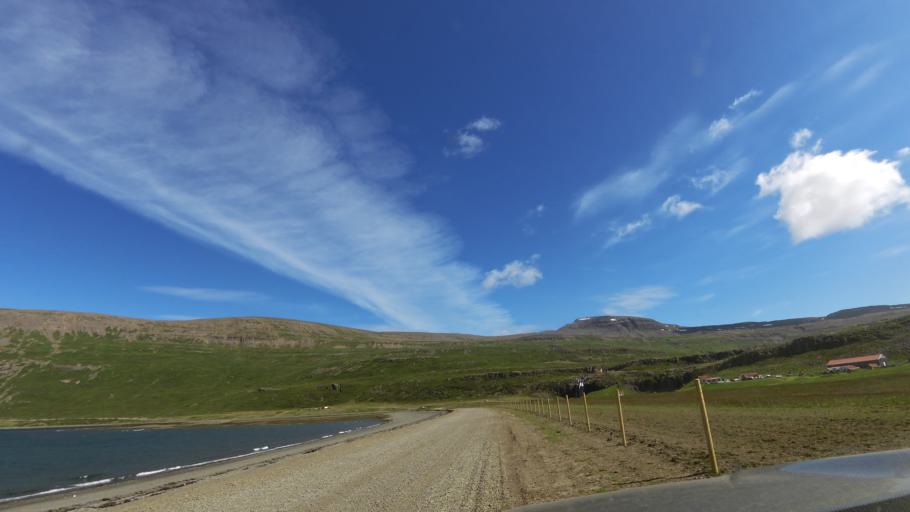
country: IS
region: Westfjords
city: Isafjoerdur
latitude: 65.6043
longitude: -23.5497
